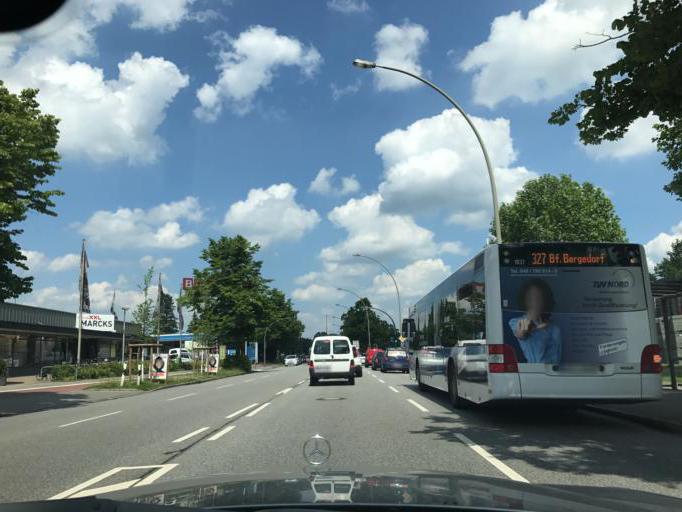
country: DE
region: Hamburg
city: Bergedorf
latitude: 53.4806
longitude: 10.2079
